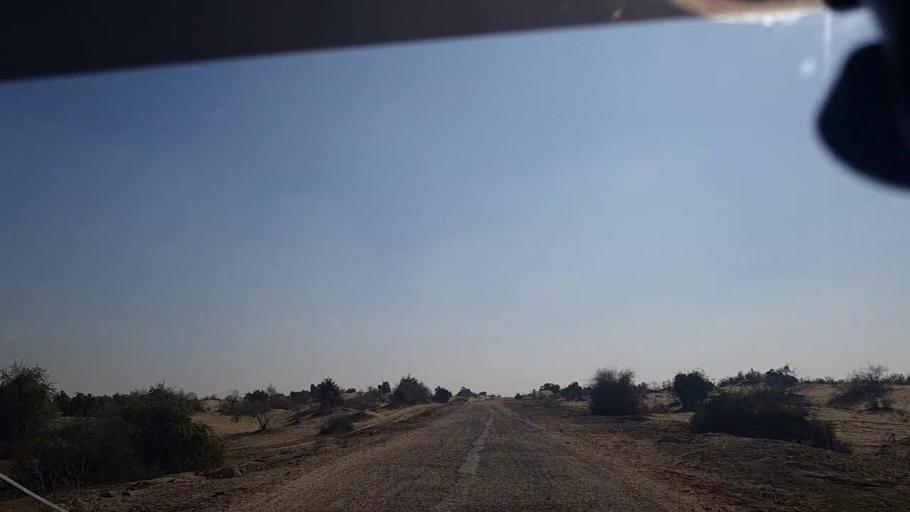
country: PK
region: Sindh
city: Khanpur
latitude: 27.5768
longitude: 69.3054
